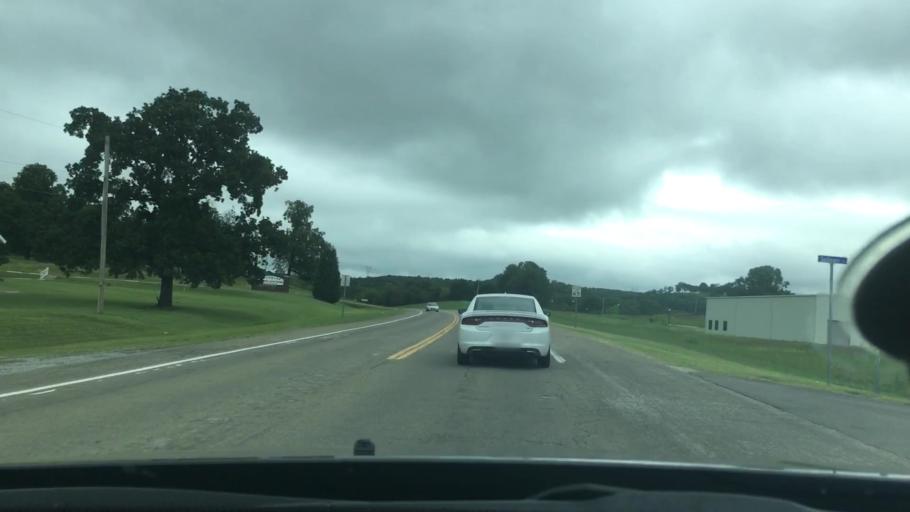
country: US
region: Oklahoma
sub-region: Sequoyah County
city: Vian
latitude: 35.5104
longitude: -94.9687
